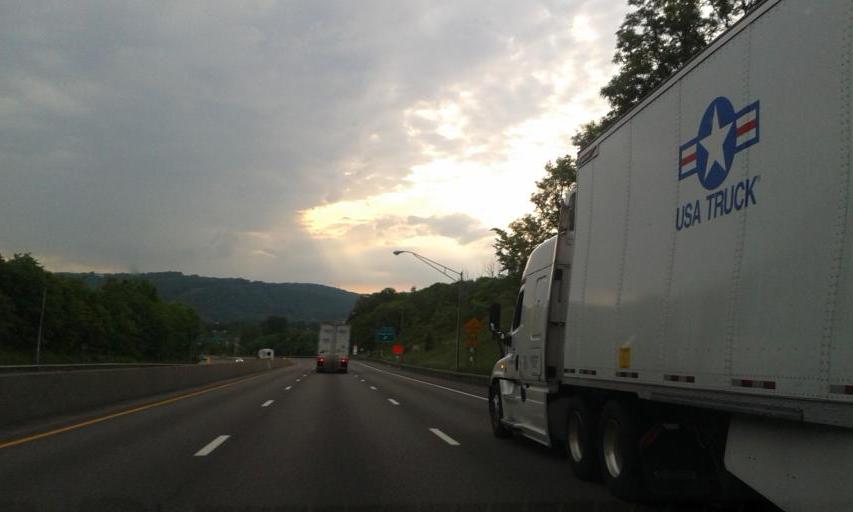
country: US
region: New York
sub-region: Broome County
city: Port Dickinson
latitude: 42.1143
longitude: -75.8819
